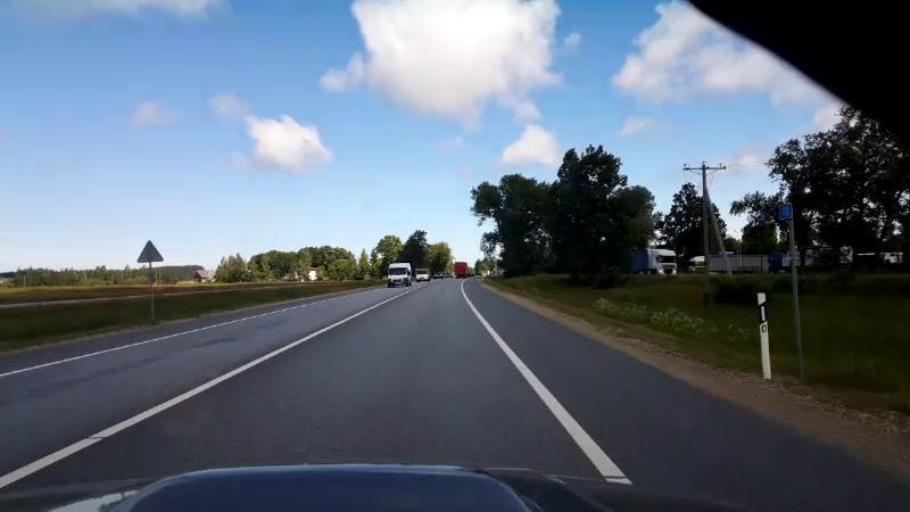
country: LV
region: Adazi
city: Adazi
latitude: 57.0987
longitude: 24.3119
